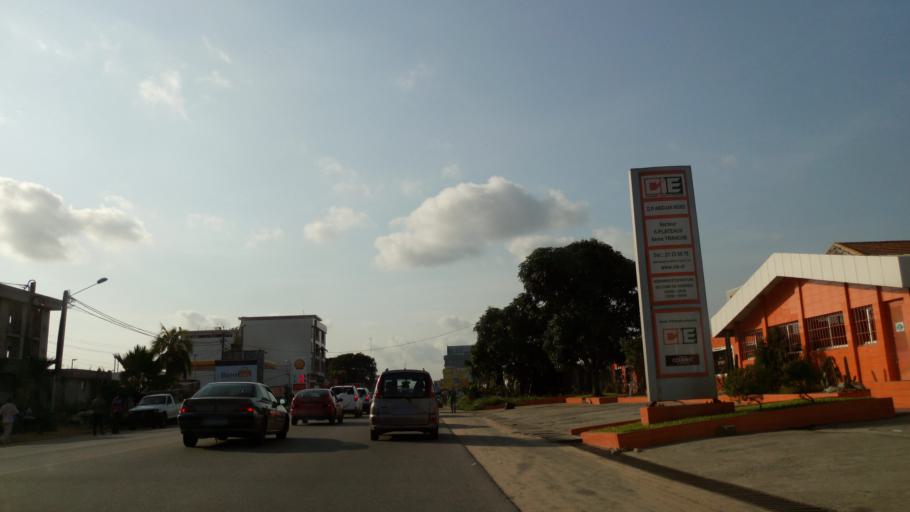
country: CI
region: Lagunes
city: Abobo
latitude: 5.3885
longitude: -3.9749
